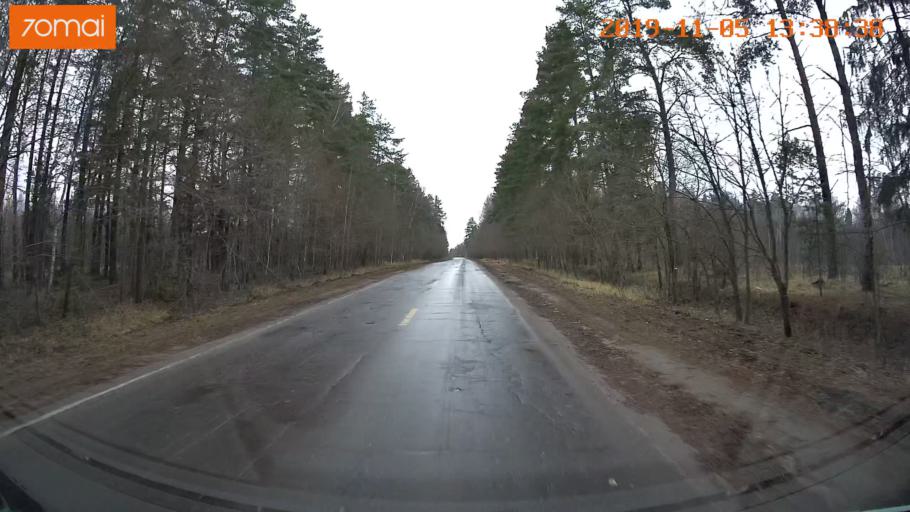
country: RU
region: Ivanovo
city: Shuya
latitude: 56.9335
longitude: 41.3868
